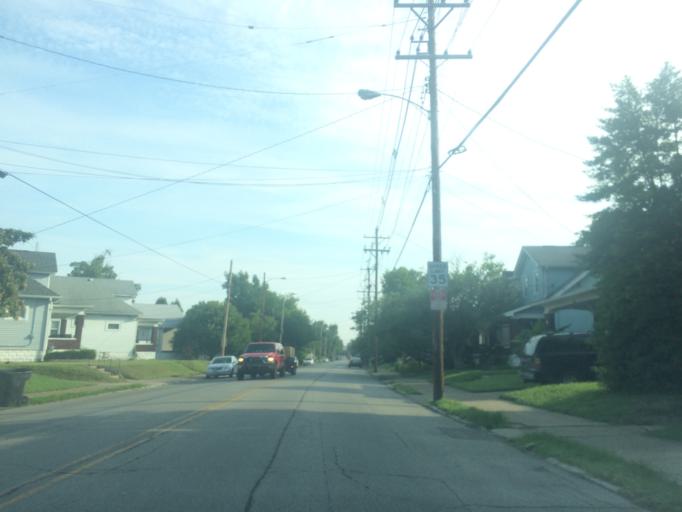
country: US
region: Kentucky
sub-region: Jefferson County
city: Audubon Park
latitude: 38.2184
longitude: -85.7439
